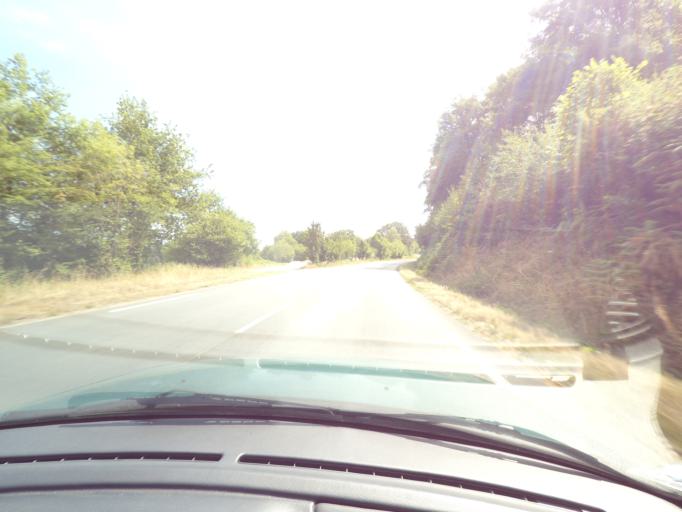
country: FR
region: Limousin
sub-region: Departement de la Haute-Vienne
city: Eymoutiers
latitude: 45.7359
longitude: 1.6825
